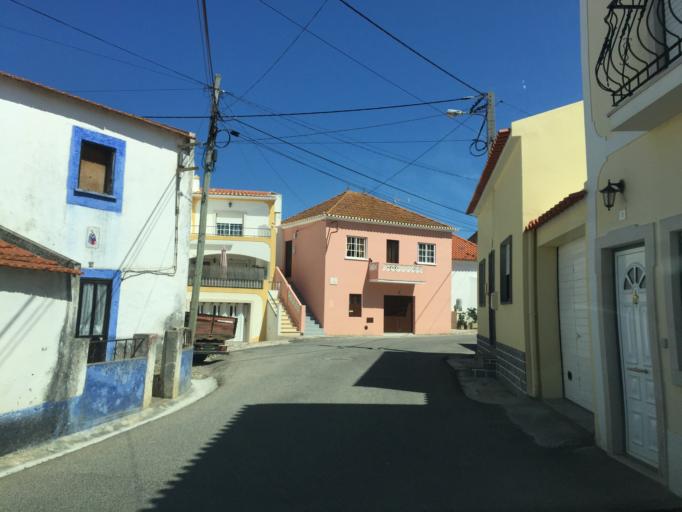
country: PT
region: Lisbon
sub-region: Lourinha
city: Lourinha
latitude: 39.2679
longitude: -9.3129
